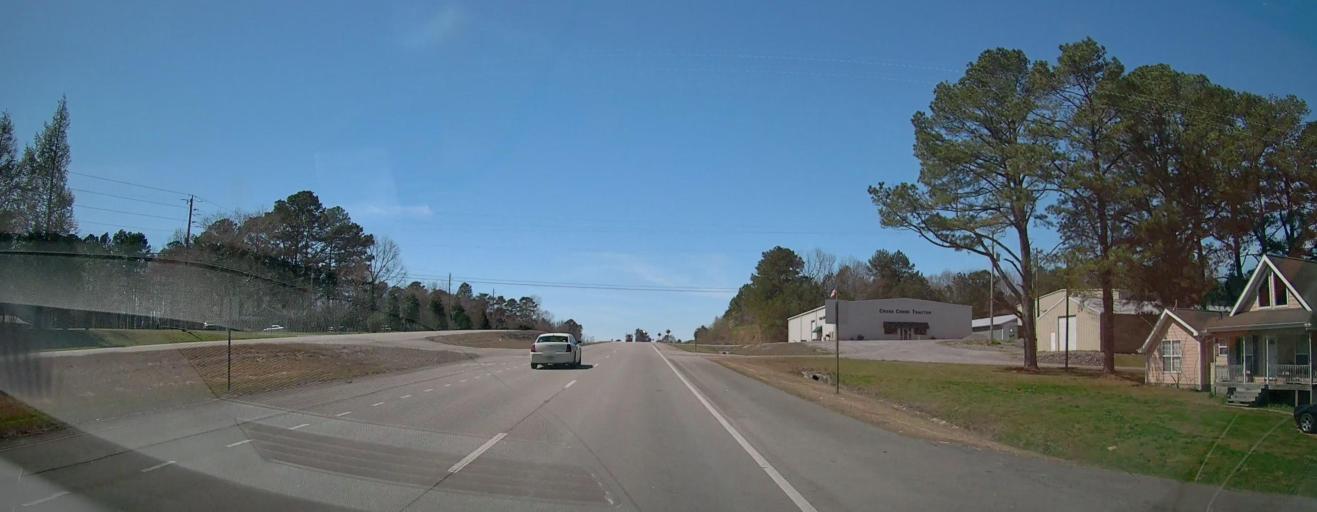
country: US
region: Alabama
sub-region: Cullman County
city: Cullman
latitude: 34.1772
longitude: -86.7295
